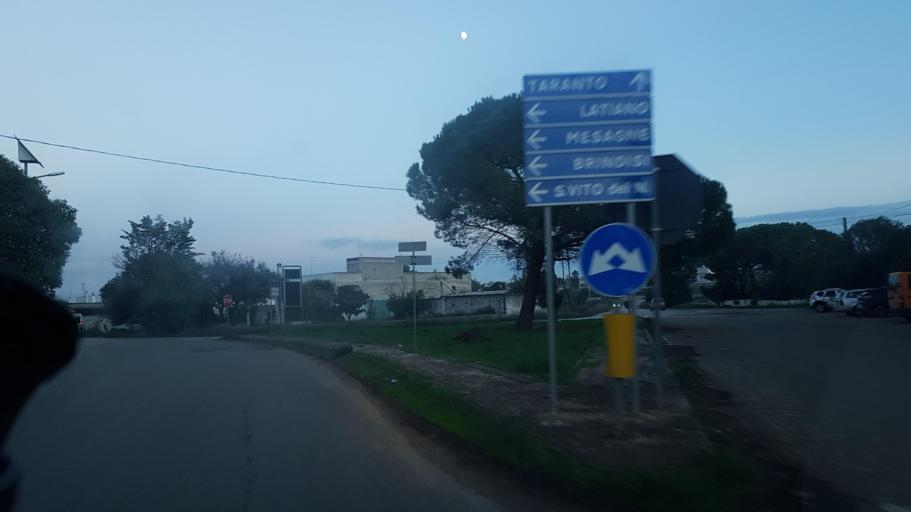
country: IT
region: Apulia
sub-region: Provincia di Brindisi
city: Latiano
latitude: 40.5595
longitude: 17.7110
